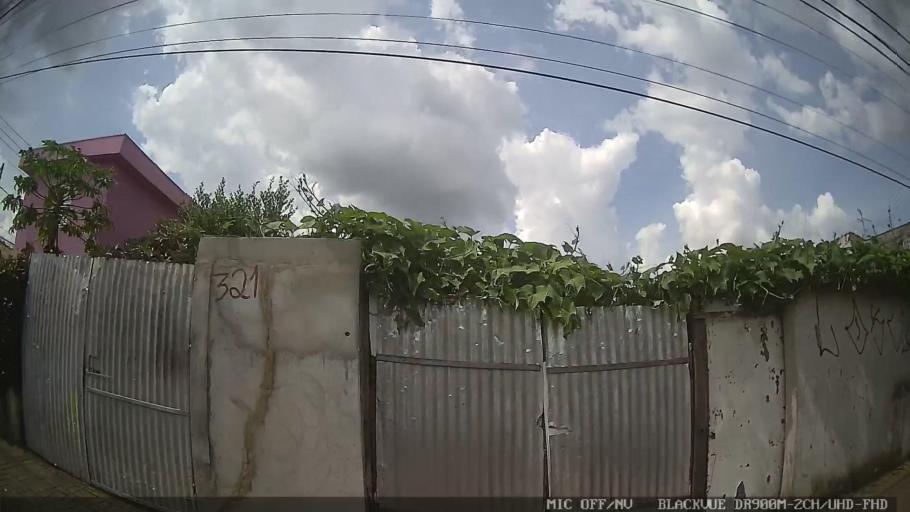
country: BR
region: Sao Paulo
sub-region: Poa
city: Poa
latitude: -23.5318
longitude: -46.3355
